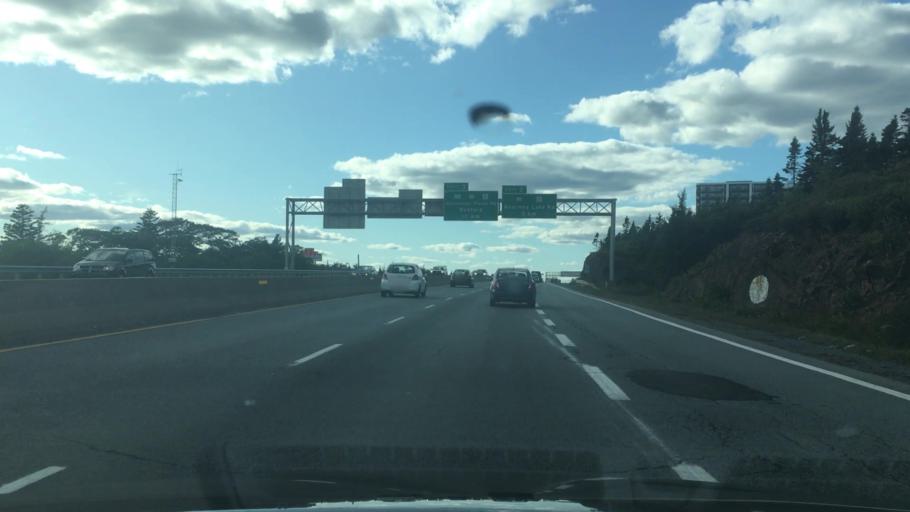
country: CA
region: Nova Scotia
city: Dartmouth
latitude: 44.6451
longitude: -63.6611
